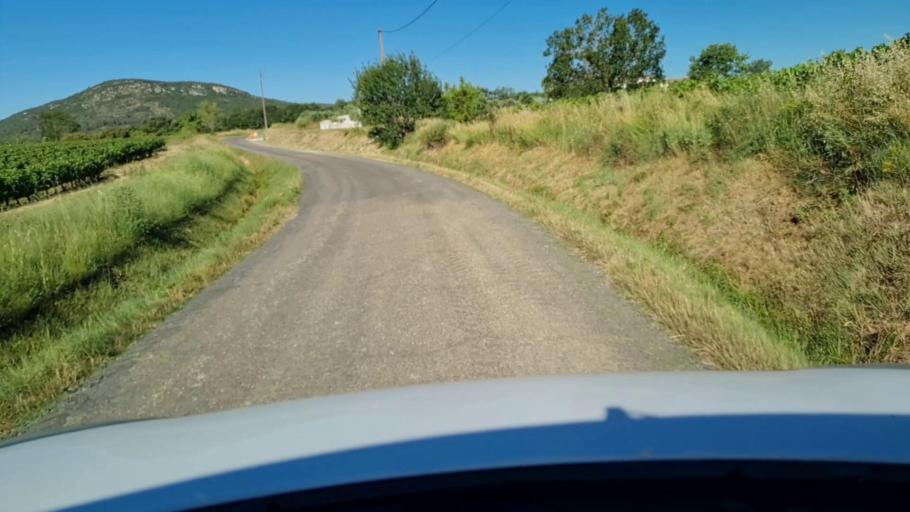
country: FR
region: Languedoc-Roussillon
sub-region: Departement du Gard
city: Sommieres
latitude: 43.8319
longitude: 4.0361
